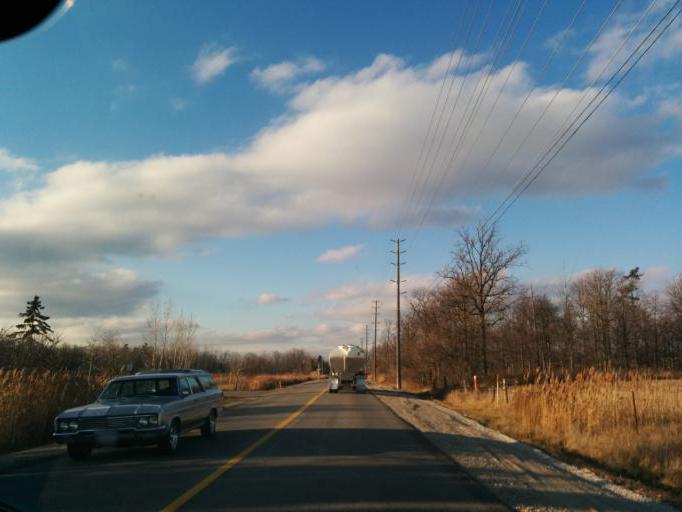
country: CA
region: Ontario
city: Oakville
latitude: 43.5157
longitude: -79.7074
